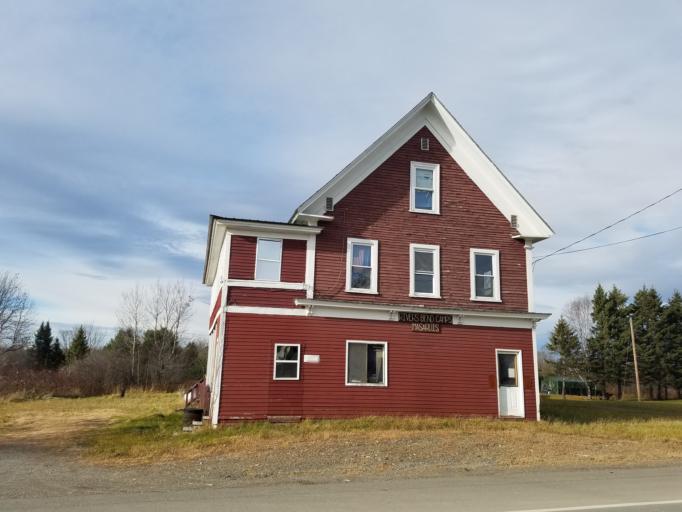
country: US
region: Maine
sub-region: Aroostook County
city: Presque Isle
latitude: 46.5020
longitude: -68.3628
